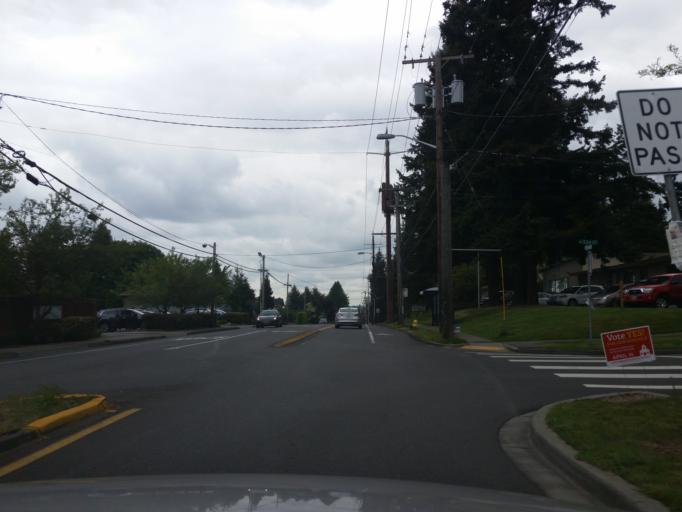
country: US
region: Washington
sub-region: King County
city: Yarrow Point
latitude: 47.6557
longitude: -122.1962
